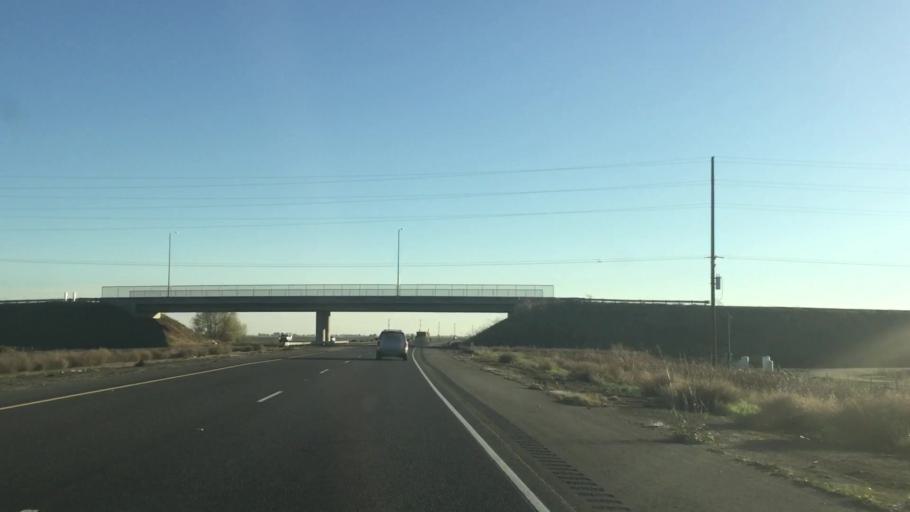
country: US
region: California
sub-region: Yuba County
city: Plumas Lake
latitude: 38.8969
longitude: -121.5446
